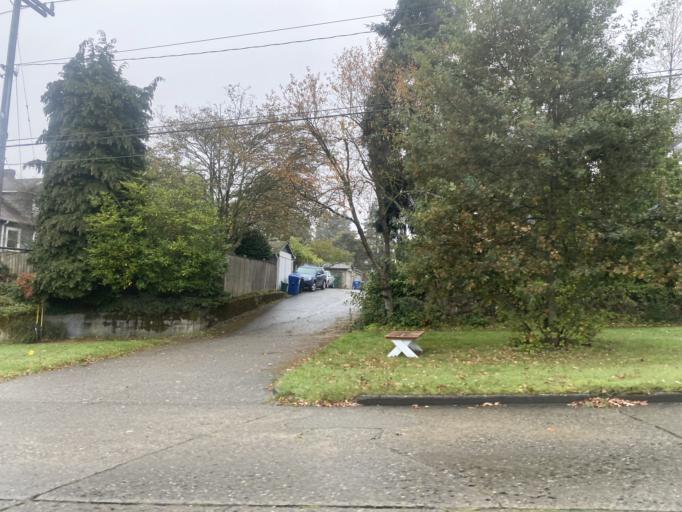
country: US
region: Washington
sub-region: King County
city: Seattle
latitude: 47.6487
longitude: -122.3909
